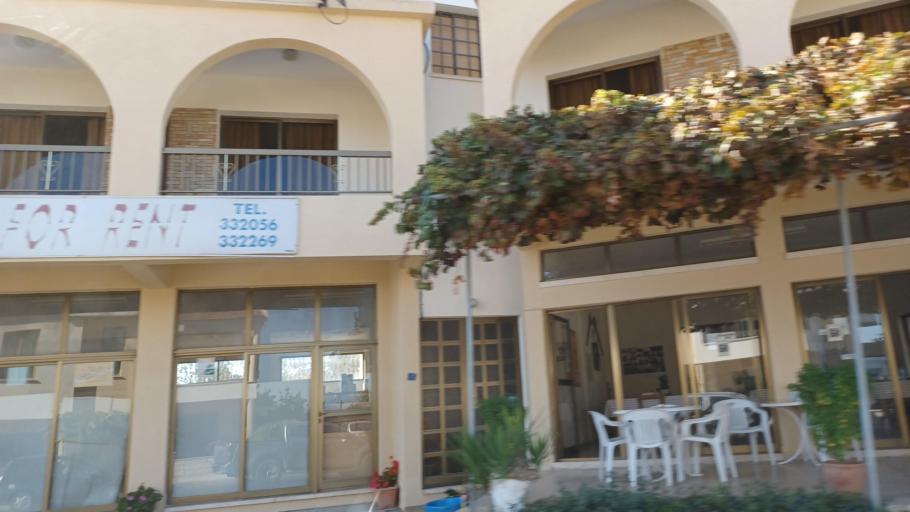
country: CY
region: Pafos
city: Pegeia
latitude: 34.9586
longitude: 32.3979
